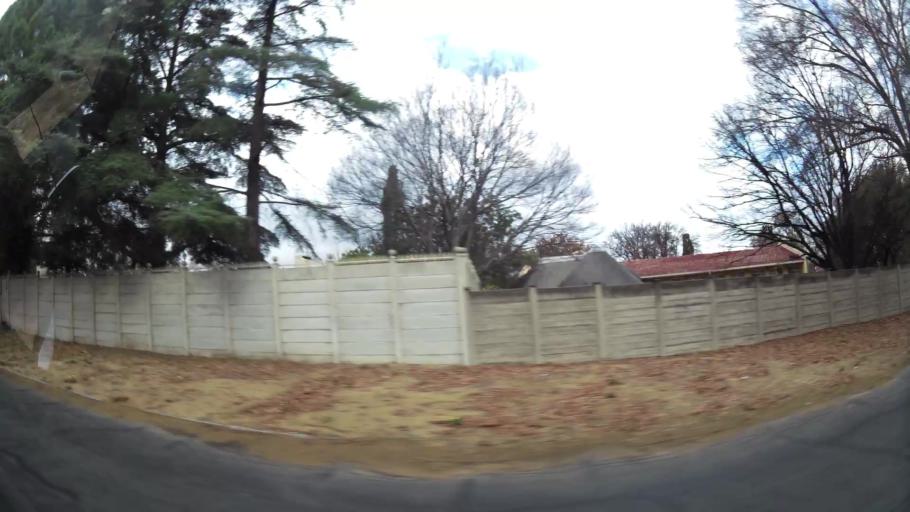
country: ZA
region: Orange Free State
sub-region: Fezile Dabi District Municipality
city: Sasolburg
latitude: -26.7927
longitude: 27.8149
